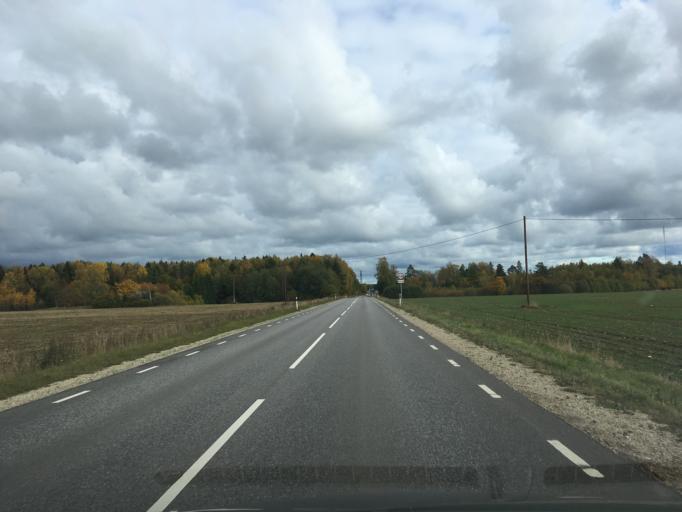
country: EE
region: Harju
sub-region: Anija vald
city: Kehra
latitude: 59.2511
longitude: 25.3155
